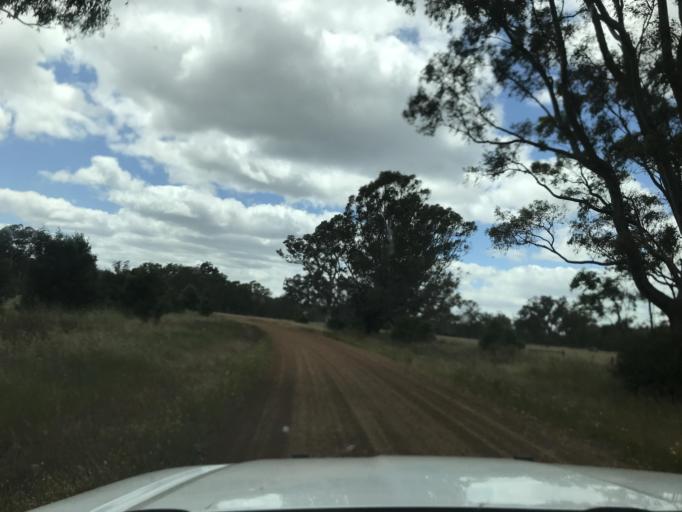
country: AU
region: South Australia
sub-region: Wattle Range
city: Penola
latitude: -37.3720
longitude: 141.2344
